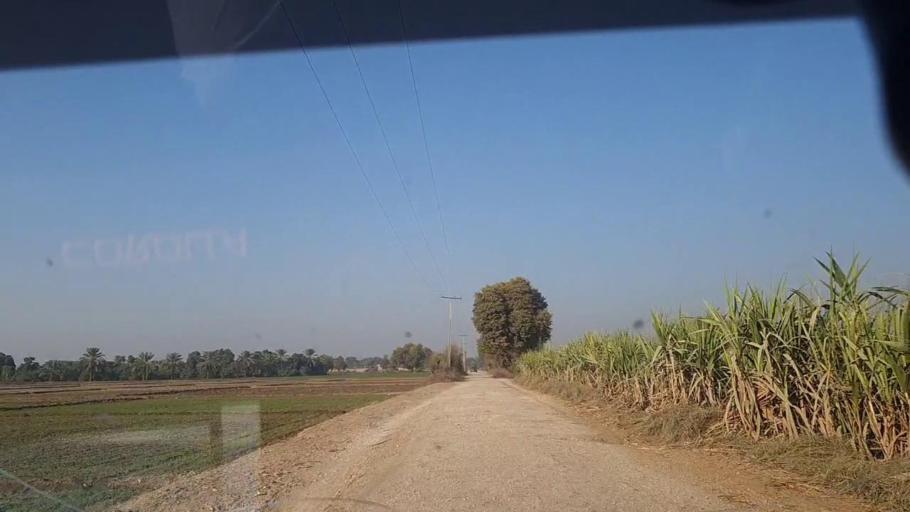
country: PK
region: Sindh
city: Sobhadero
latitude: 27.2501
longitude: 68.3500
